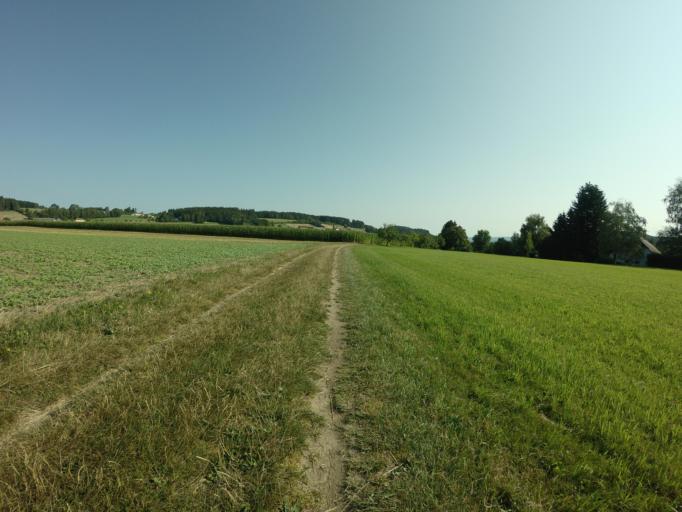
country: AT
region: Upper Austria
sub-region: Politischer Bezirk Urfahr-Umgebung
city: Bad Leonfelden
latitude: 48.5393
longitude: 14.3142
